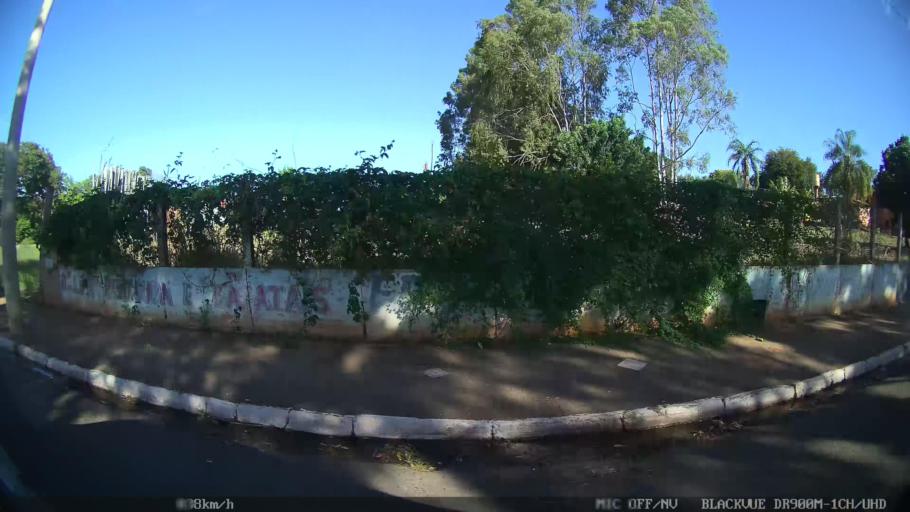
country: BR
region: Sao Paulo
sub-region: Olimpia
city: Olimpia
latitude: -20.7443
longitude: -48.9064
